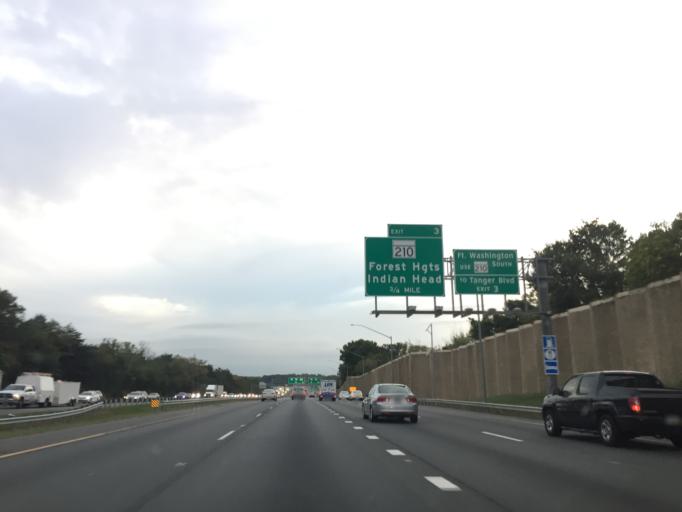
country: US
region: Maryland
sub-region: Prince George's County
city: Oxon Hill
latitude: 38.8073
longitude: -76.9806
